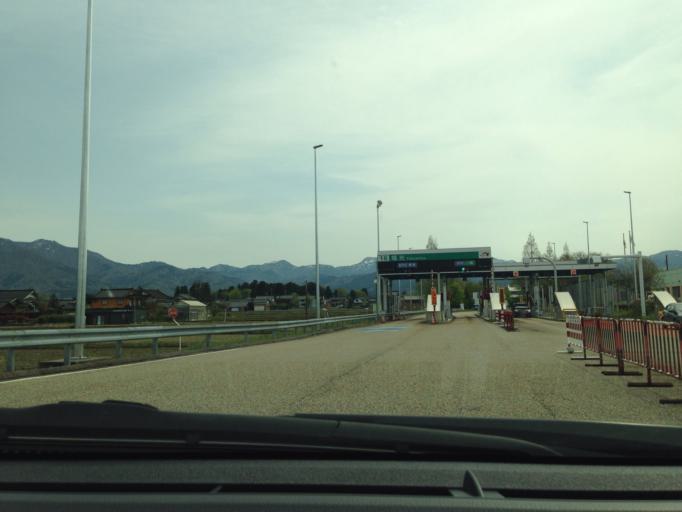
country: JP
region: Toyama
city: Fukumitsu
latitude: 36.5330
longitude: 136.8896
